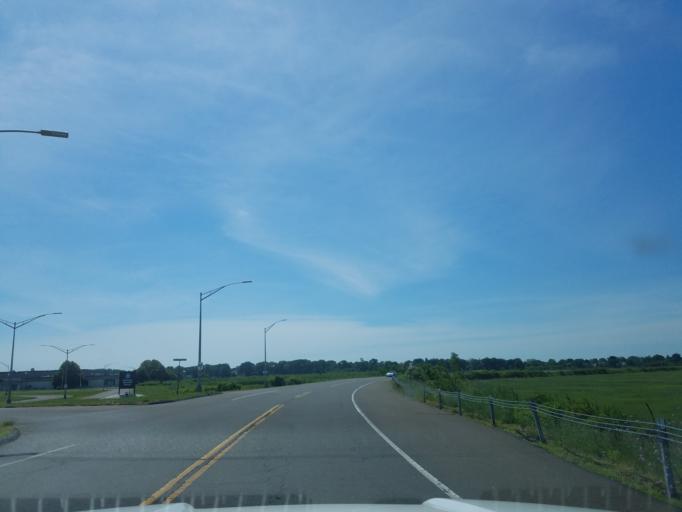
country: US
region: Connecticut
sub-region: Fairfield County
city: Stratford
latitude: 41.1623
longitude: -73.1345
